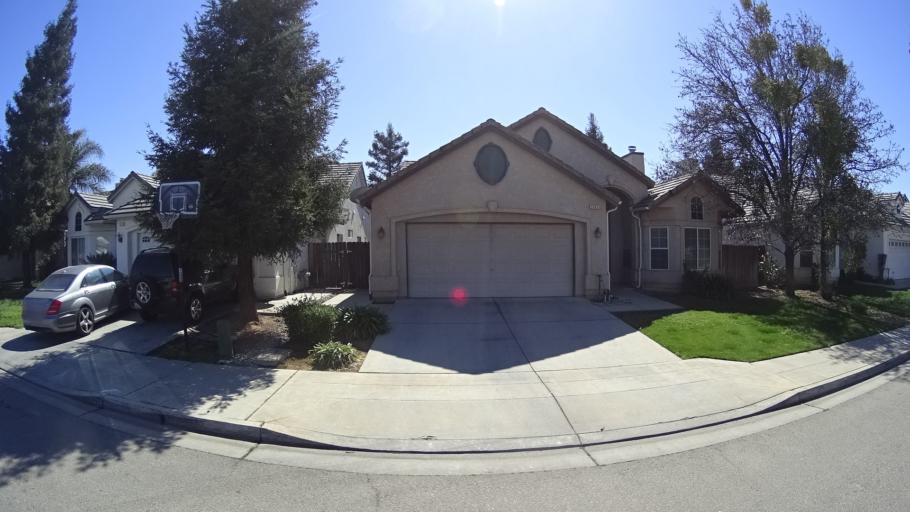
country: US
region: California
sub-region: Fresno County
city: Clovis
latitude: 36.8788
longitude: -119.7326
